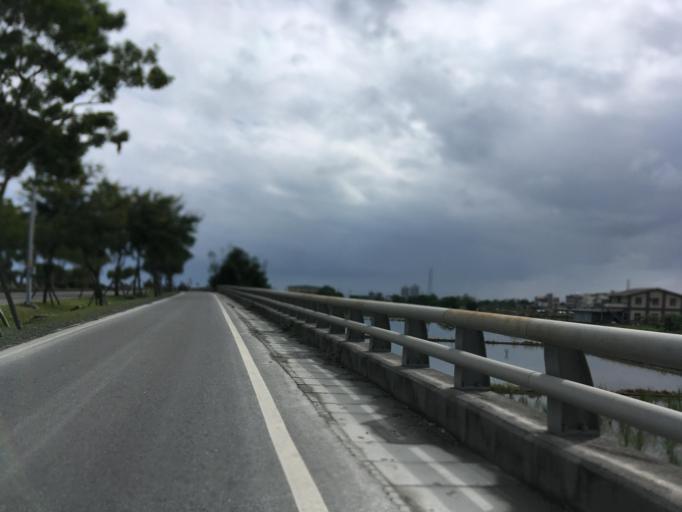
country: TW
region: Taiwan
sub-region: Yilan
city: Yilan
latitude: 24.6777
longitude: 121.7818
